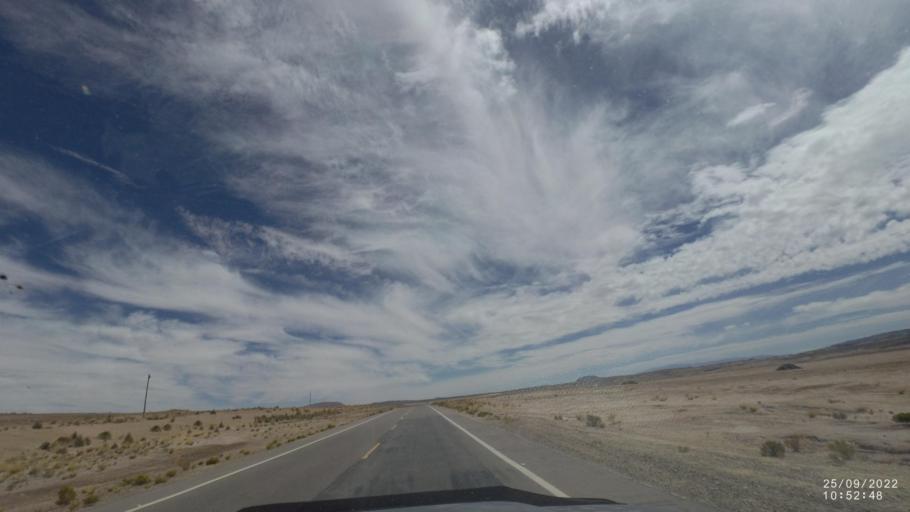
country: BO
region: Oruro
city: Challapata
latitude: -19.5427
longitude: -66.8549
